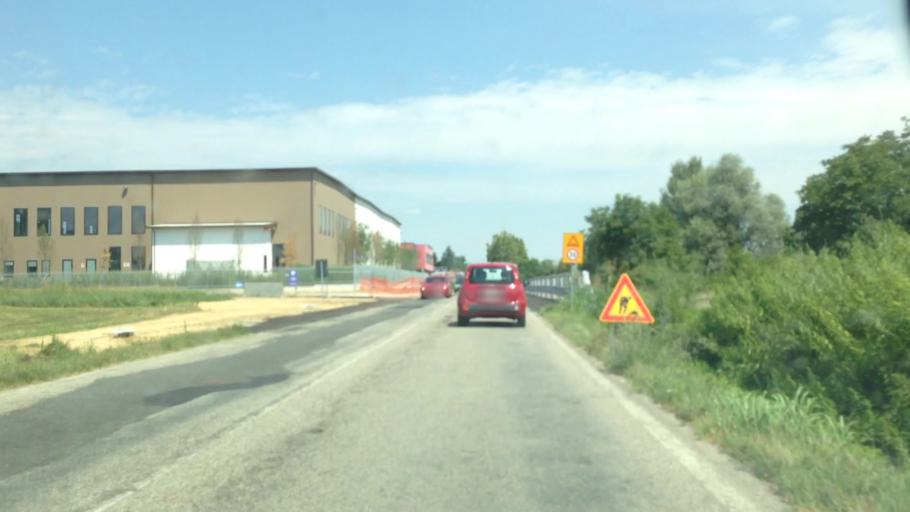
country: IT
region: Piedmont
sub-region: Provincia di Asti
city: Asti
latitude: 44.9361
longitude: 8.2249
